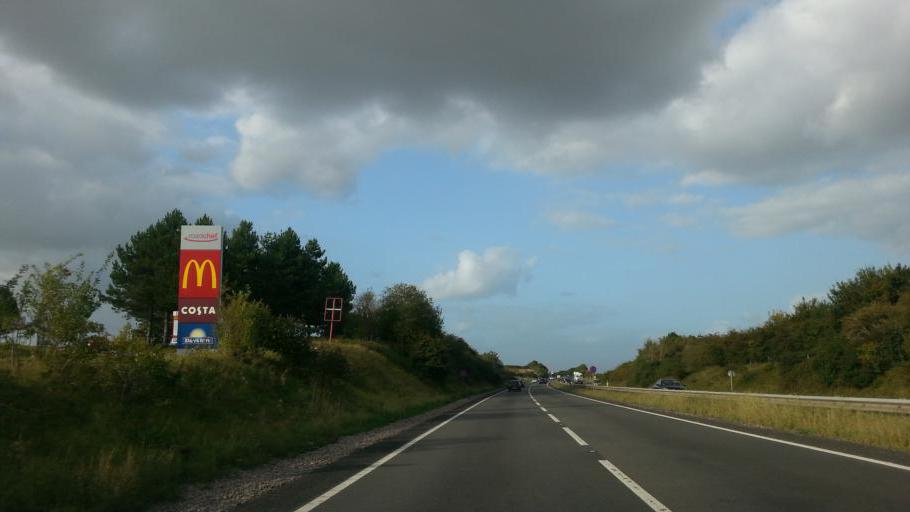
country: GB
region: England
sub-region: Hampshire
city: Kings Worthy
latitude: 51.1555
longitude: -1.3459
